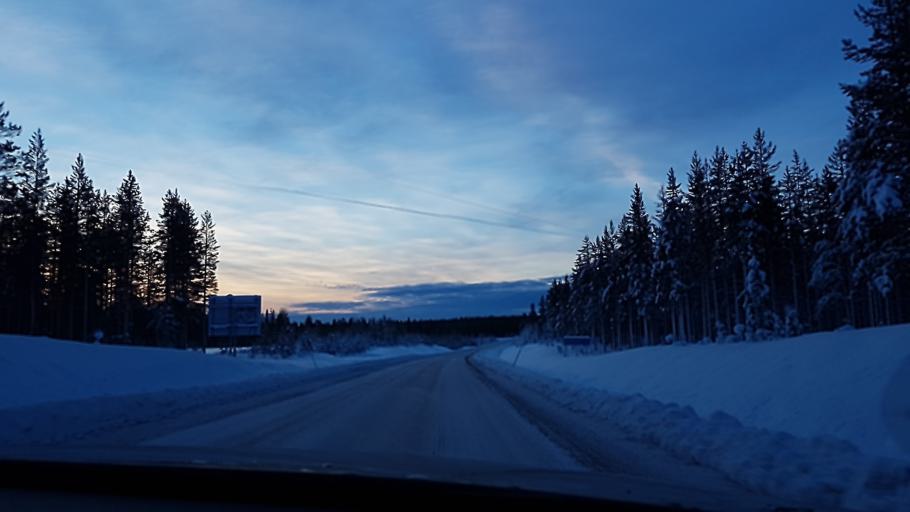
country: SE
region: Norrbotten
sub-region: Jokkmokks Kommun
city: Jokkmokk
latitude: 66.0661
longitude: 20.0763
